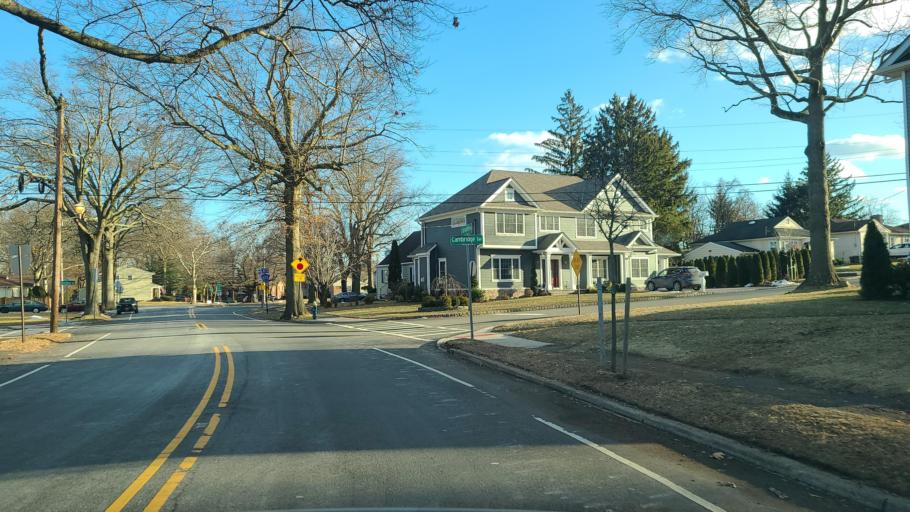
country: US
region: New Jersey
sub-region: Union County
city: Springfield
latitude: 40.6960
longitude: -74.3204
